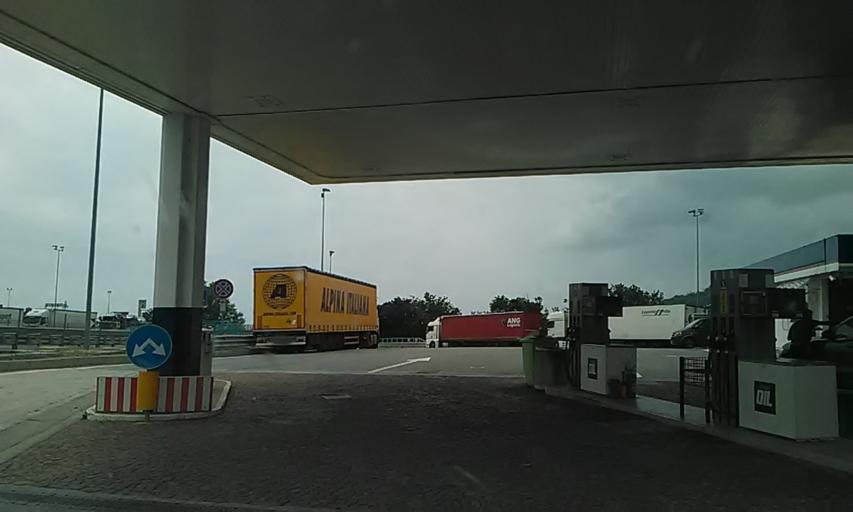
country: IT
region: Liguria
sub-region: Provincia di Genova
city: Mele
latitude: 44.4552
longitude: 8.7444
